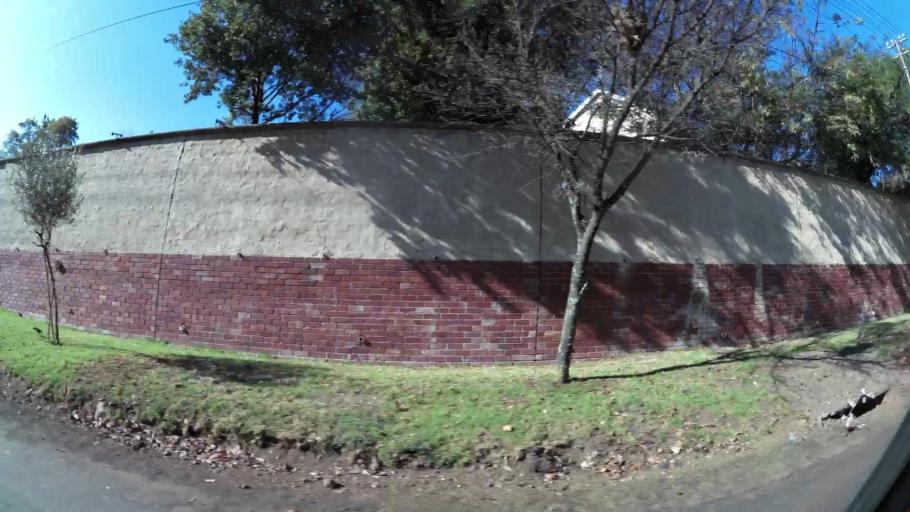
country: ZA
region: Gauteng
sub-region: City of Johannesburg Metropolitan Municipality
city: Johannesburg
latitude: -26.1223
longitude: 28.0181
